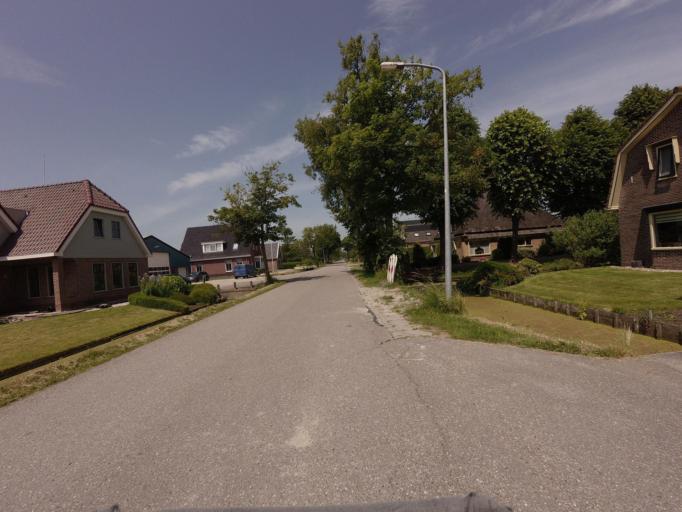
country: NL
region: North Holland
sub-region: Gemeente Opmeer
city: Opmeer
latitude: 52.6562
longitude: 4.9374
